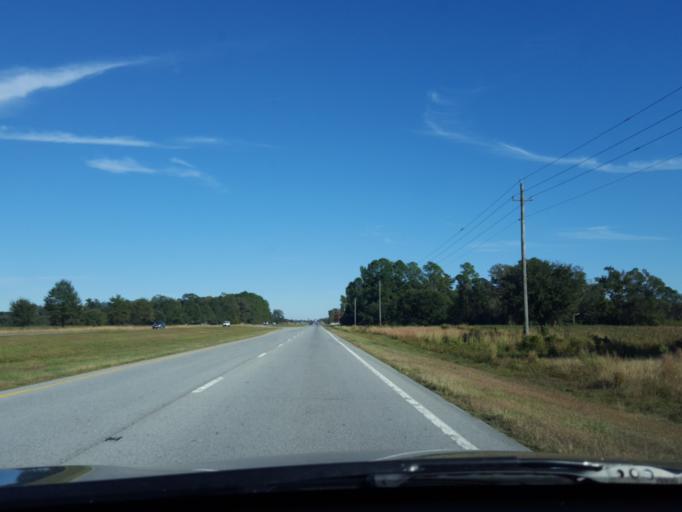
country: US
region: North Carolina
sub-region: Pitt County
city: Greenville
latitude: 35.6256
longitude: -77.2880
